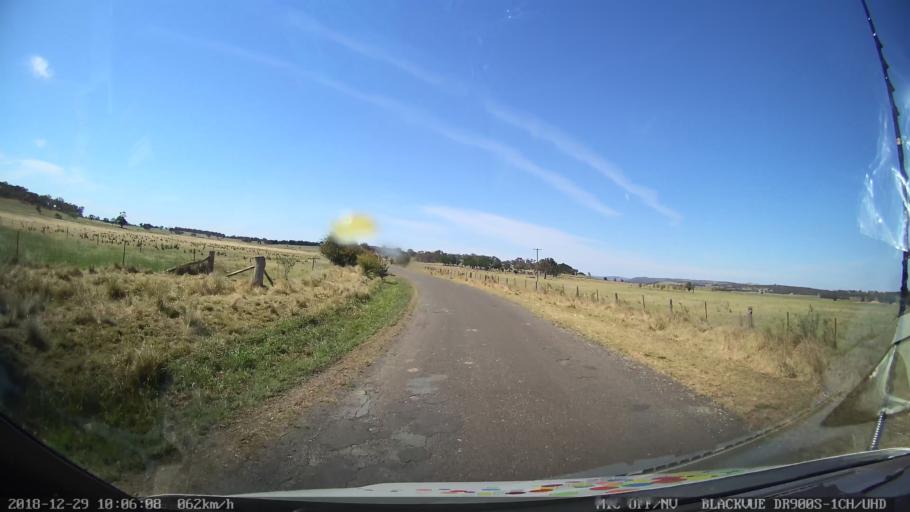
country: AU
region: New South Wales
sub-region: Goulburn Mulwaree
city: Goulburn
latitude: -34.8401
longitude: 149.4544
